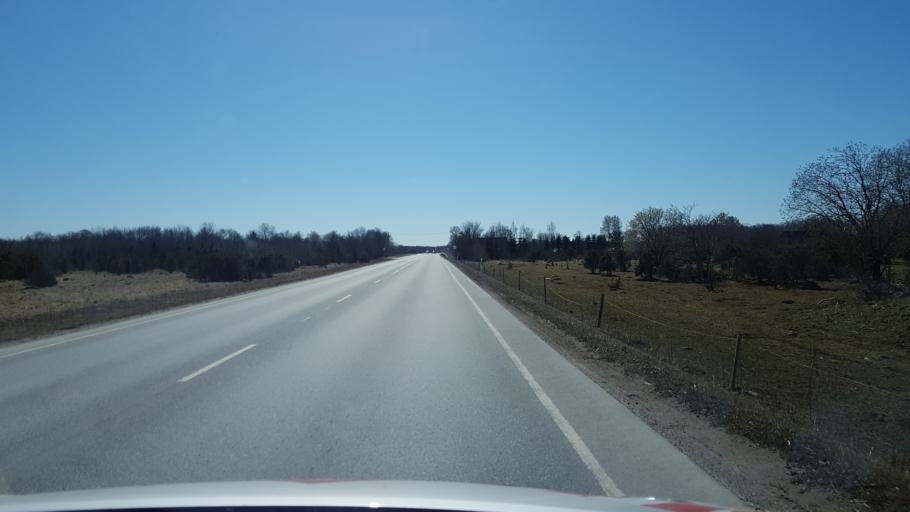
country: EE
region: Laeaene-Virumaa
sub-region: Viru-Nigula vald
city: Kunda
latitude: 59.4744
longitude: 26.4834
